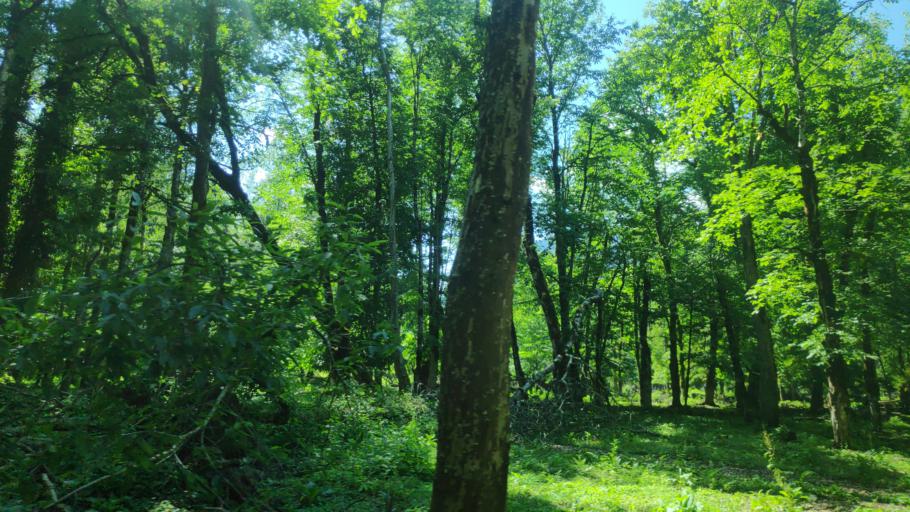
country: GE
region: Abkhazia
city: Gagra
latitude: 43.4806
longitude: 40.5626
